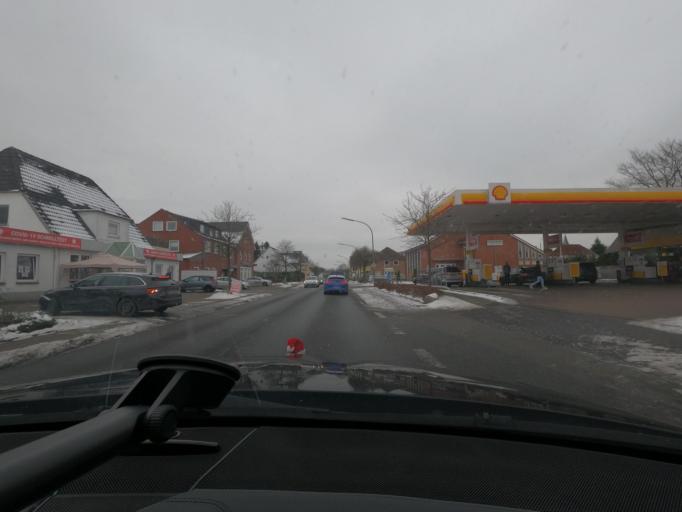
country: DE
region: Schleswig-Holstein
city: Jarplund-Weding
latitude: 54.7561
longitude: 9.4018
